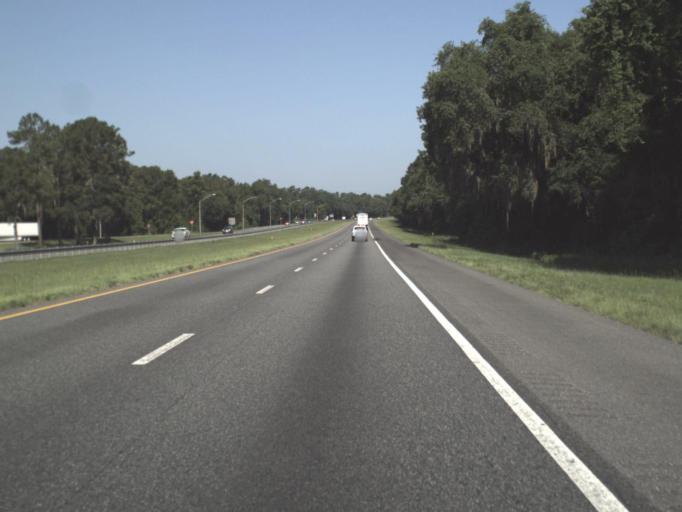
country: US
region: Florida
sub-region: Suwannee County
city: Wellborn
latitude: 30.2749
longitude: -82.7987
